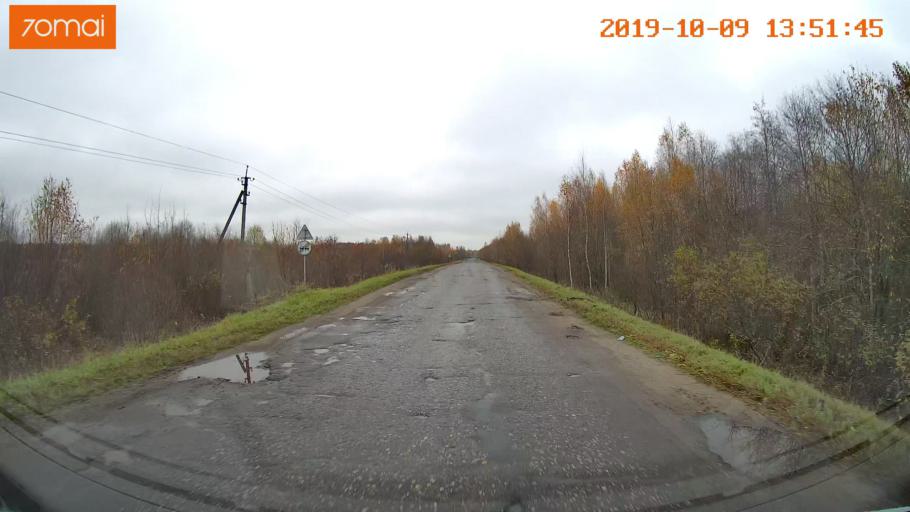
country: RU
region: Kostroma
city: Buy
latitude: 58.4091
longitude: 41.2418
